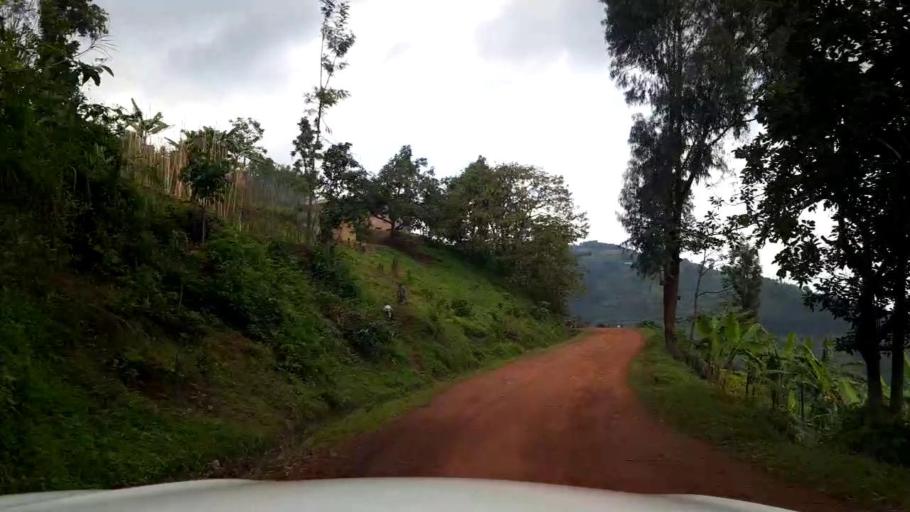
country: UG
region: Western Region
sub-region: Kisoro District
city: Kisoro
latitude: -1.3909
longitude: 29.7976
